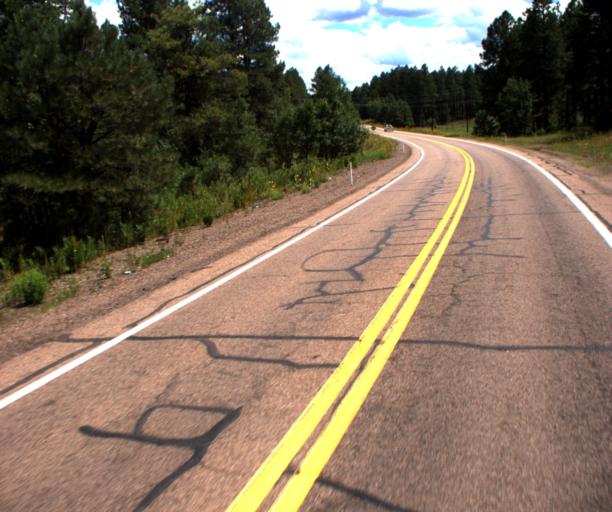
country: US
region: Arizona
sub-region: Navajo County
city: Pinetop-Lakeside
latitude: 34.0800
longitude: -109.8687
